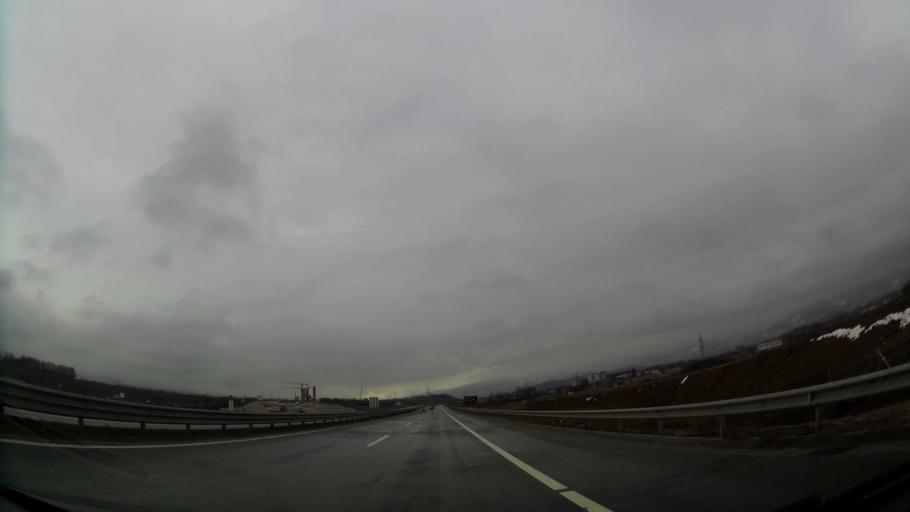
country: XK
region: Ferizaj
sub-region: Komuna e Kacanikut
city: Kacanik
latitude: 42.2829
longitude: 21.2092
